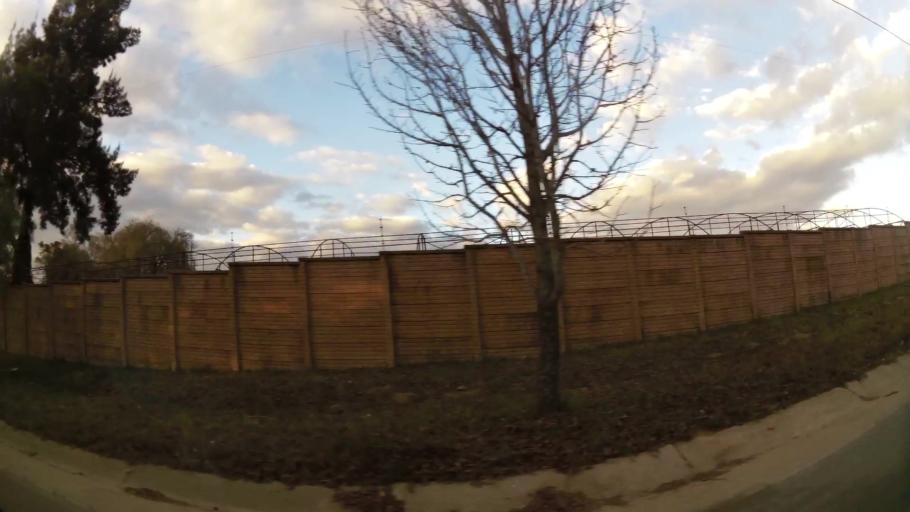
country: ZA
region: Gauteng
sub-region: City of Johannesburg Metropolitan Municipality
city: Midrand
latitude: -26.0128
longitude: 28.1566
